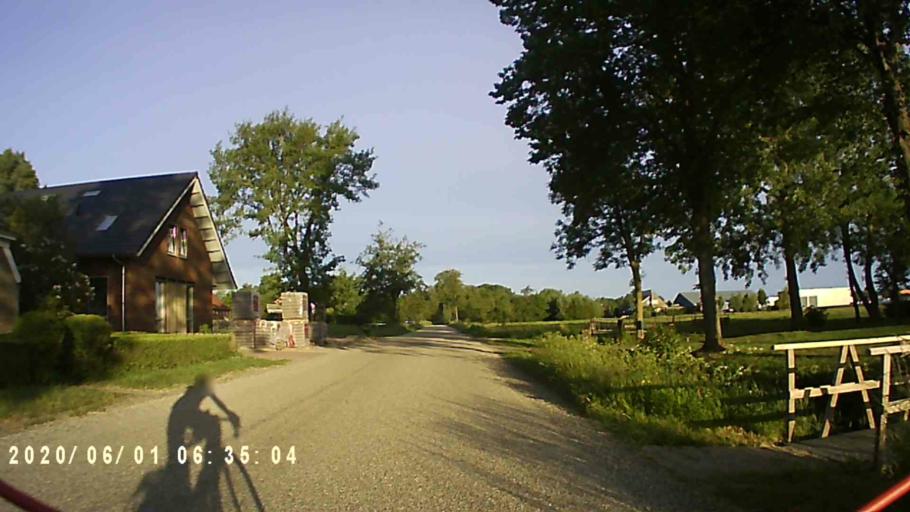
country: NL
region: Friesland
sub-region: Gemeente Kollumerland en Nieuwkruisland
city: Kollum
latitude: 53.2801
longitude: 6.1647
